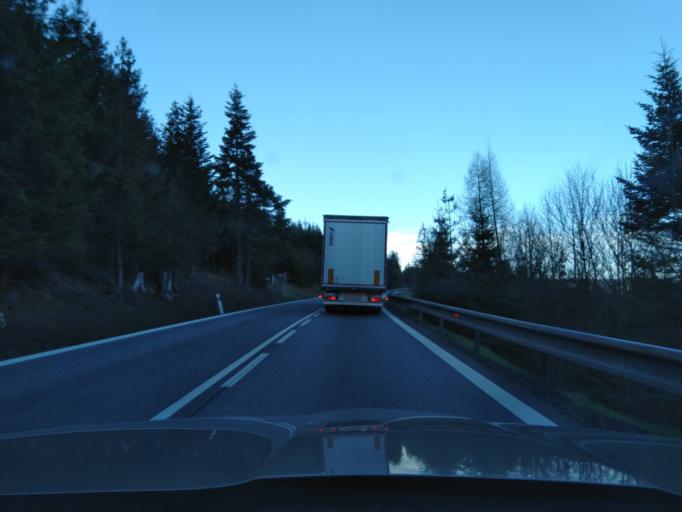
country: CZ
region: Jihocesky
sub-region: Okres Prachatice
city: Vimperk
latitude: 49.0456
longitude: 13.7612
